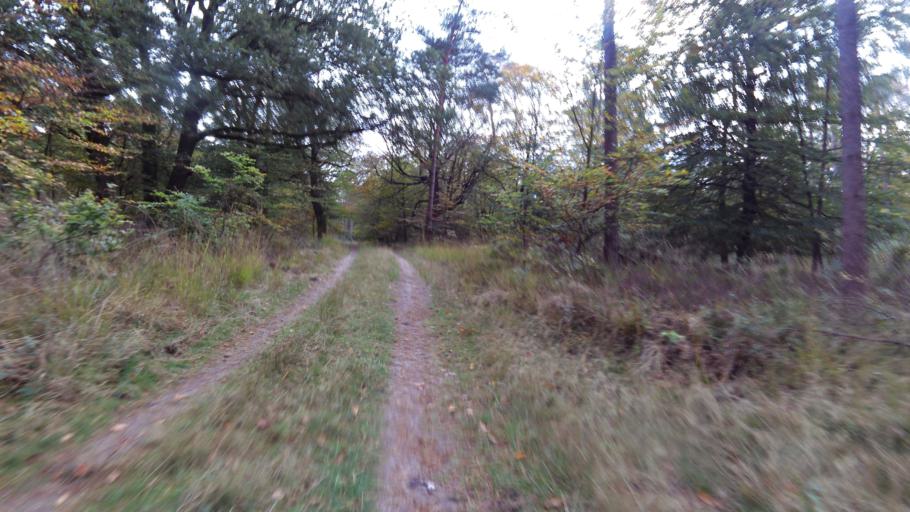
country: NL
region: Gelderland
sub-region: Gemeente Epe
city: Vaassen
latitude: 52.3200
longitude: 5.8758
